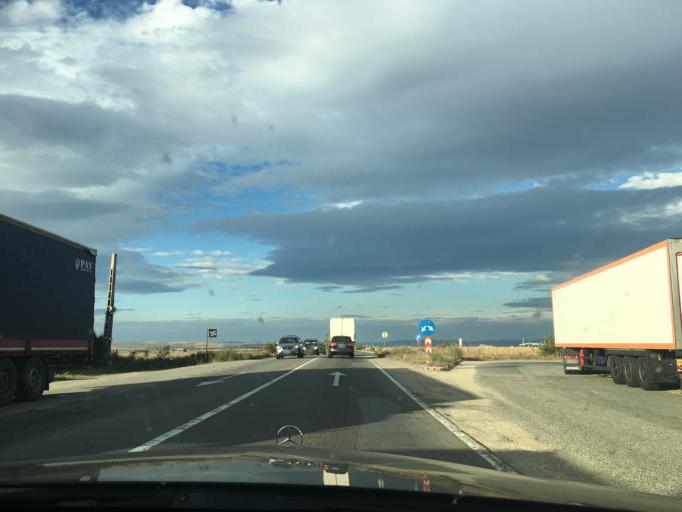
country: RO
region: Alba
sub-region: Comuna Santimbru
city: Santimbru
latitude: 46.1646
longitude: 23.6474
